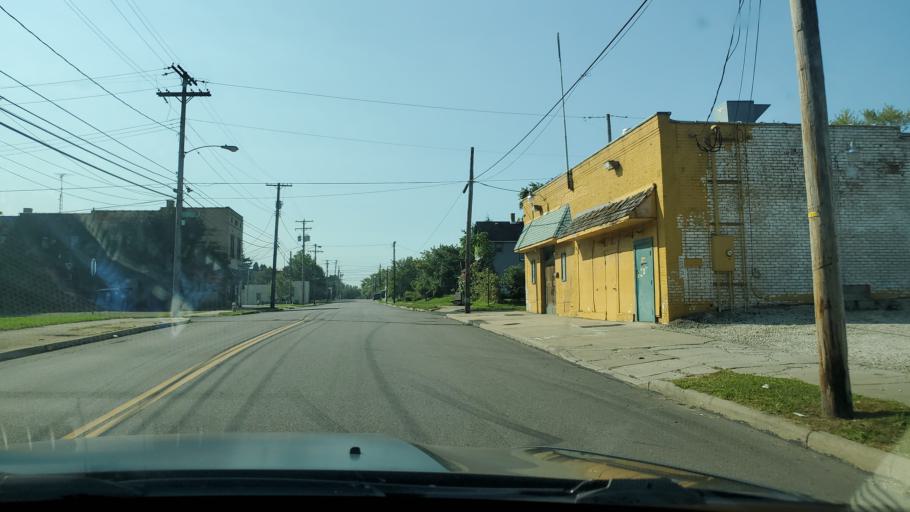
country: US
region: Ohio
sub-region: Mahoning County
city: Youngstown
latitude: 41.1105
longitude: -80.6828
